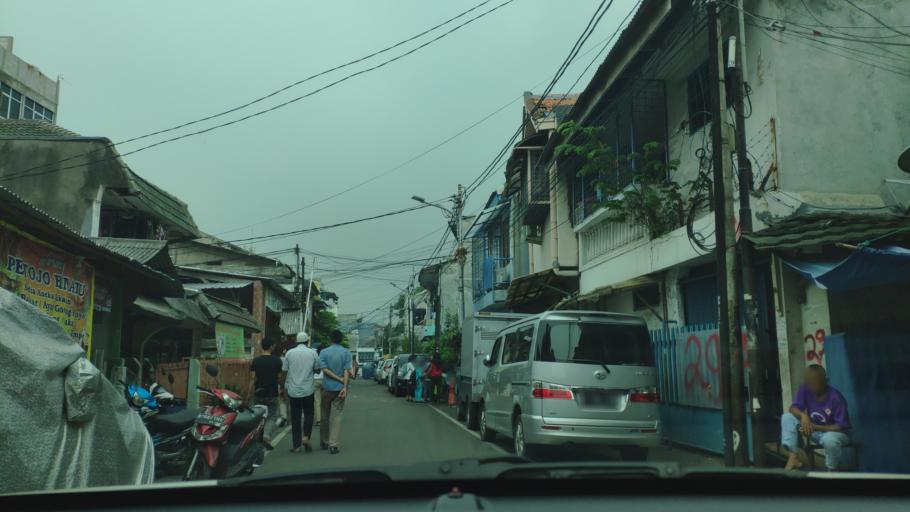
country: ID
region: Jakarta Raya
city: Jakarta
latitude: -6.1667
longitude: 106.8162
